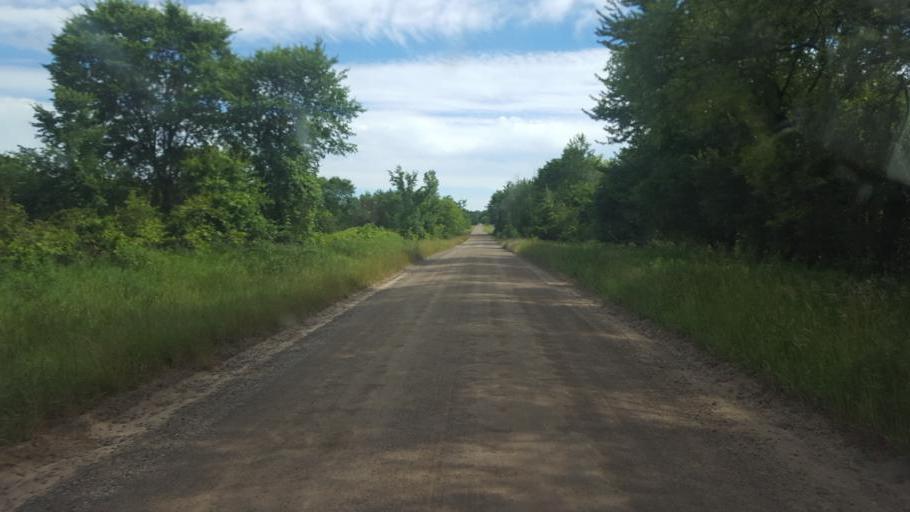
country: US
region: Michigan
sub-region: Barry County
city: Nashville
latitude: 42.5784
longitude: -84.9750
